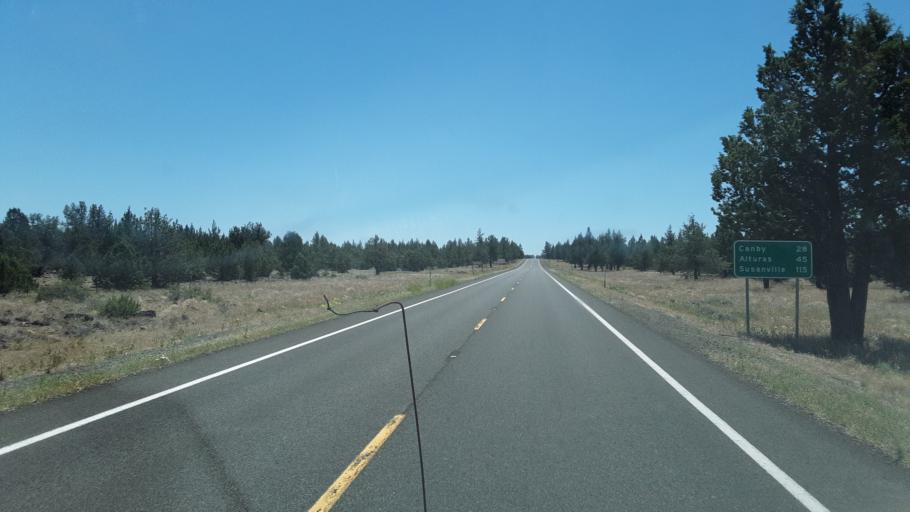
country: US
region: California
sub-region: Siskiyou County
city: Tulelake
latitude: 41.6693
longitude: -121.2561
